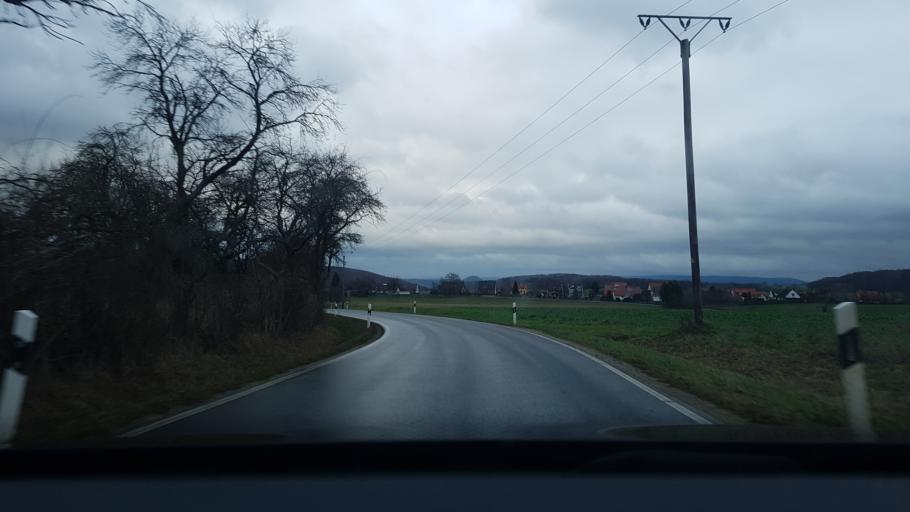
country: DE
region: Lower Saxony
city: Juhnde
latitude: 51.4077
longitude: 9.8358
